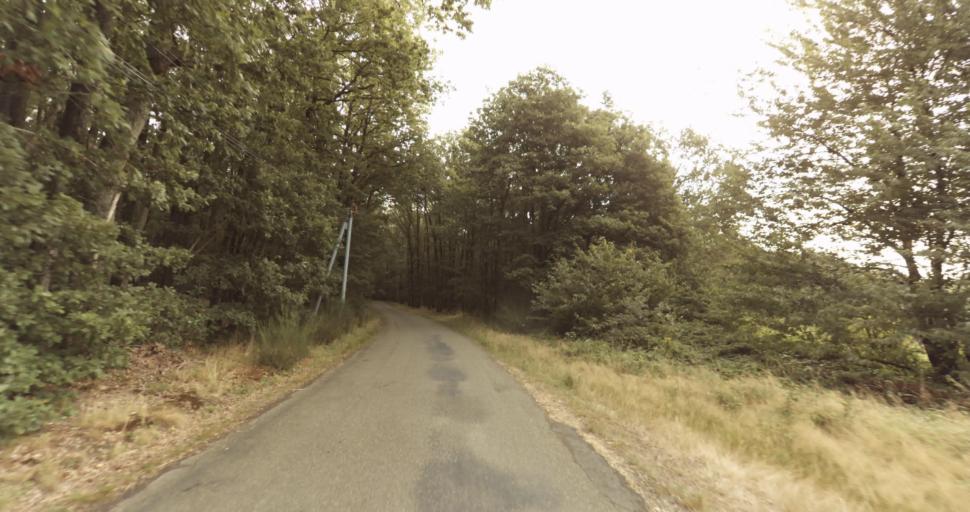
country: FR
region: Centre
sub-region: Departement d'Eure-et-Loir
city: Vert-en-Drouais
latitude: 48.7916
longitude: 1.2957
